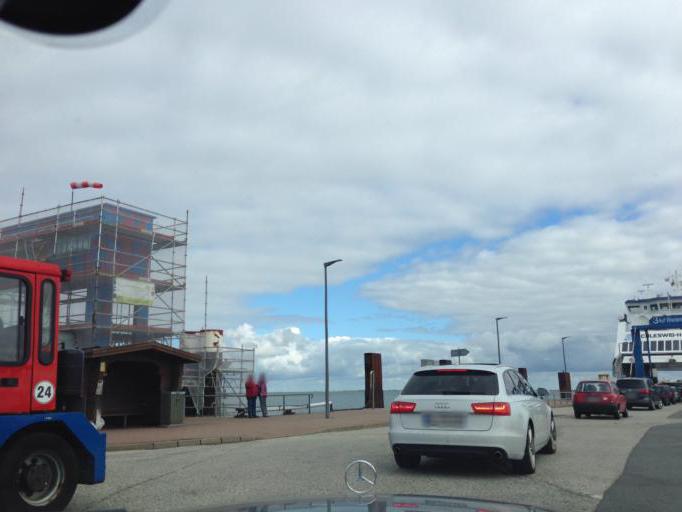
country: DE
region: Schleswig-Holstein
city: Wyk auf Fohr
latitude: 54.6927
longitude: 8.5753
